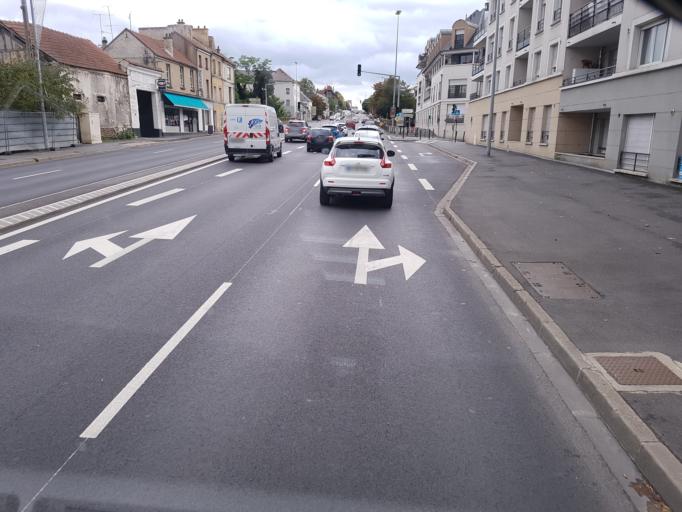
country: FR
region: Ile-de-France
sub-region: Departement de Seine-et-Marne
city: Meaux
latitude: 48.9538
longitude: 2.8793
